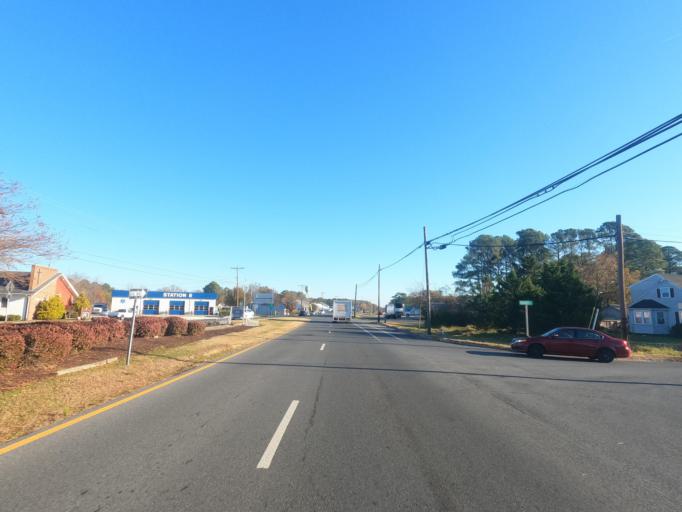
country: US
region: Maryland
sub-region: Somerset County
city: Crisfield
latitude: 37.9919
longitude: -75.8425
